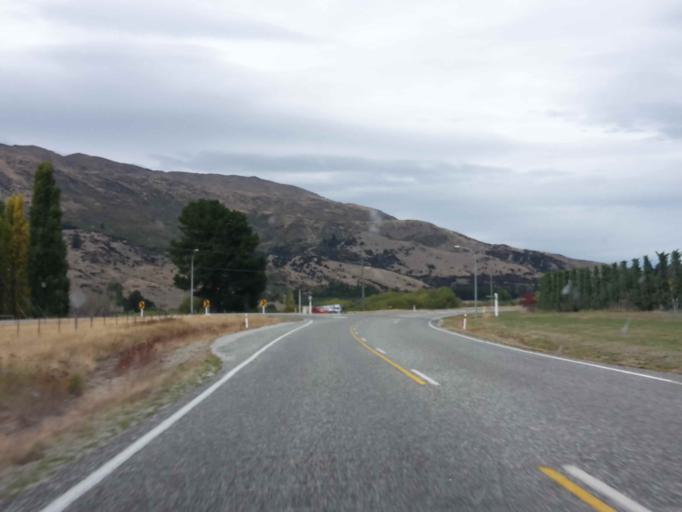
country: NZ
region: Otago
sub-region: Queenstown-Lakes District
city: Wanaka
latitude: -44.7332
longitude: 169.1364
